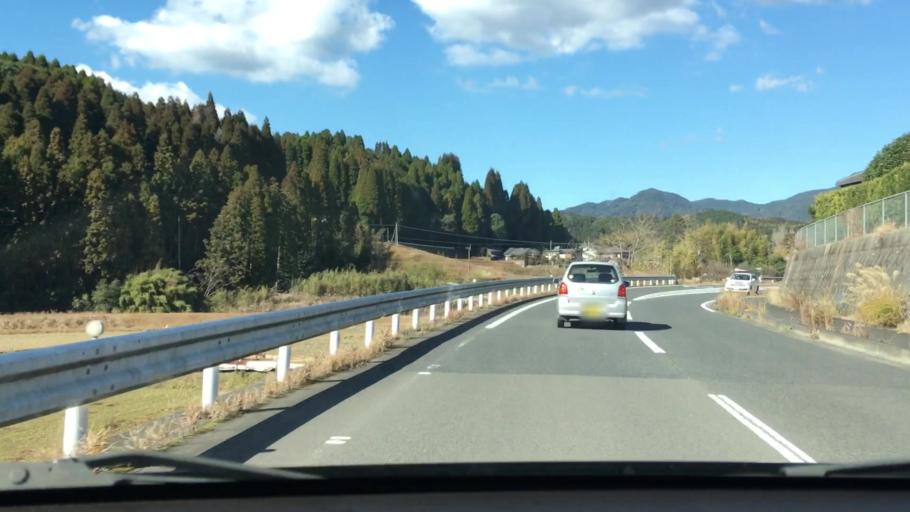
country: JP
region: Kagoshima
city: Ijuin
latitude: 31.6934
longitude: 130.4623
